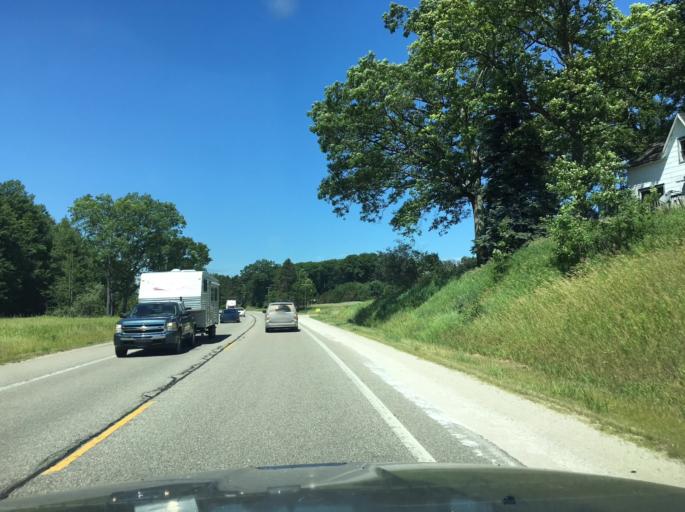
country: US
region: Michigan
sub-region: Osceola County
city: Reed City
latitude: 43.8919
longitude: -85.6556
